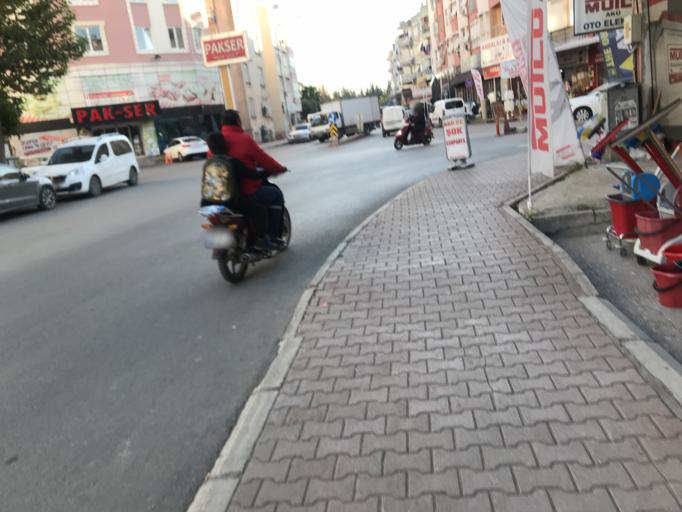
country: TR
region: Antalya
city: Antalya
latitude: 36.8976
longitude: 30.7074
